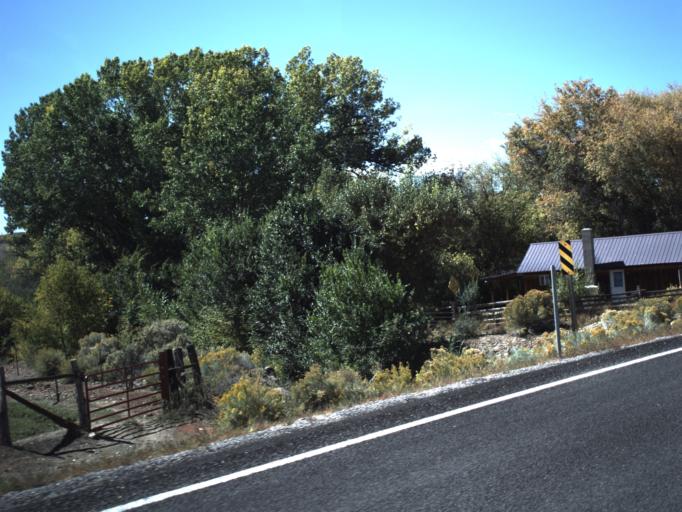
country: US
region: Utah
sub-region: Piute County
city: Junction
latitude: 38.1152
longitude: -111.9993
